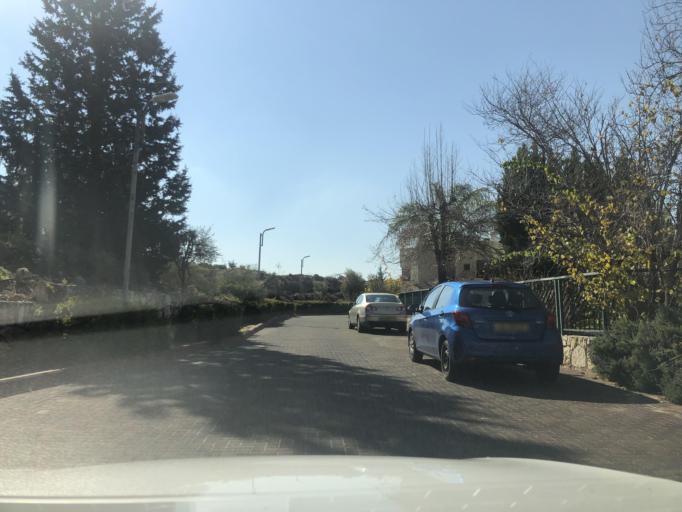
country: PS
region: West Bank
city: Mashah
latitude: 32.1093
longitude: 35.0379
